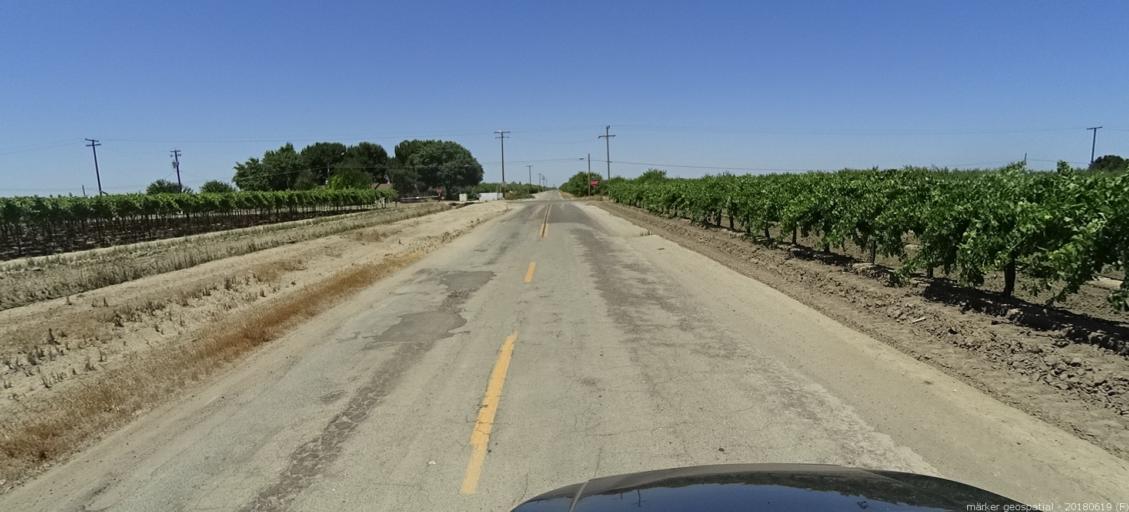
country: US
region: California
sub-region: Madera County
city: Parkwood
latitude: 36.8730
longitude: -120.0912
